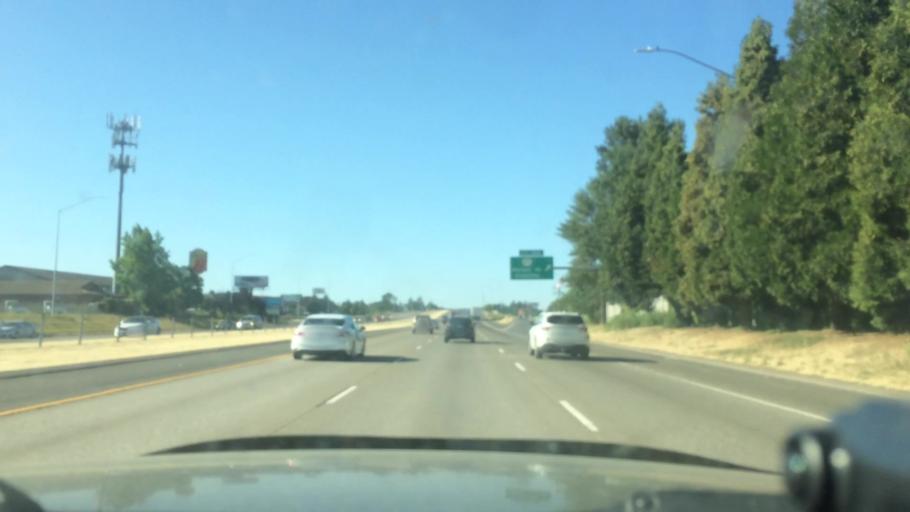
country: US
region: Oregon
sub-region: Marion County
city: Four Corners
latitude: 44.9444
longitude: -122.9902
